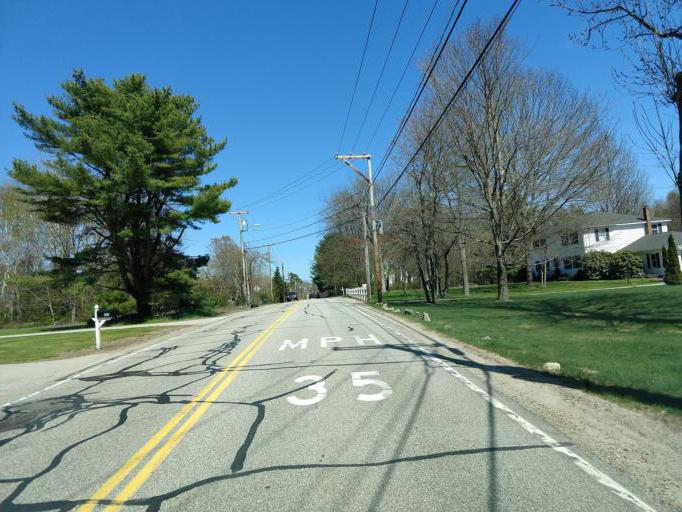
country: US
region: Maine
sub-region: York County
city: Kennebunkport
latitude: 43.3548
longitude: -70.5044
